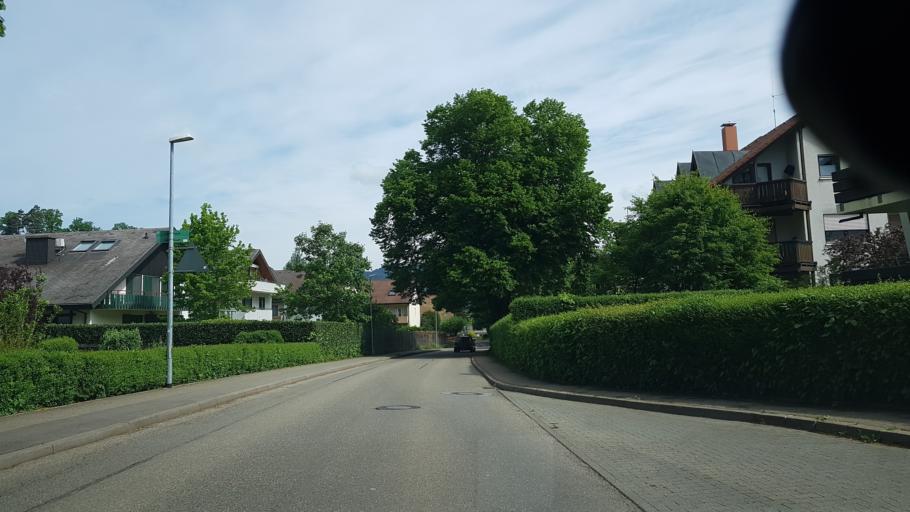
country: DE
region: Baden-Wuerttemberg
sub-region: Freiburg Region
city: Kirchzarten
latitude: 47.9712
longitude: 7.9109
